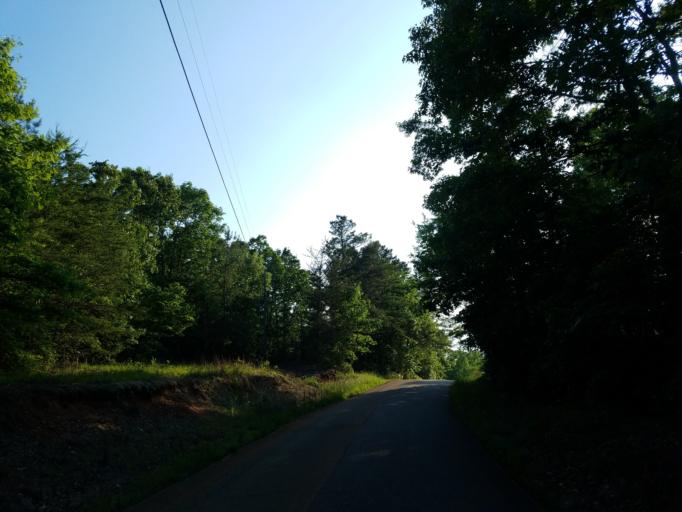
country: US
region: Georgia
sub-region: Cherokee County
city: Ball Ground
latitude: 34.3411
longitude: -84.3302
